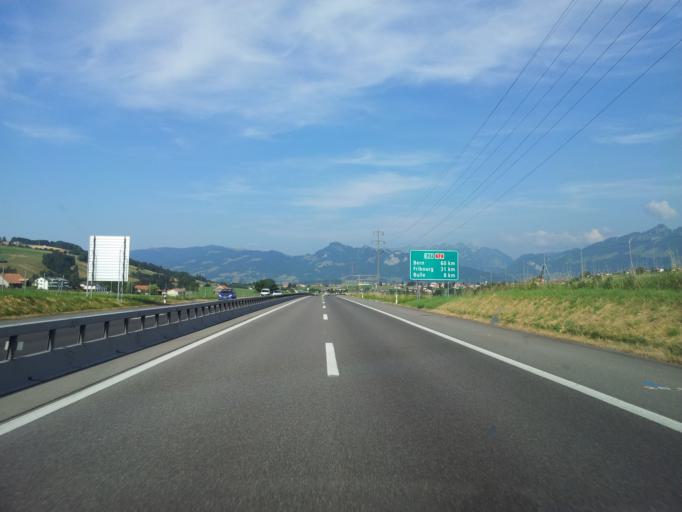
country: CH
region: Fribourg
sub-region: Gruyere District
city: Sales
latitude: 46.6171
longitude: 6.9868
